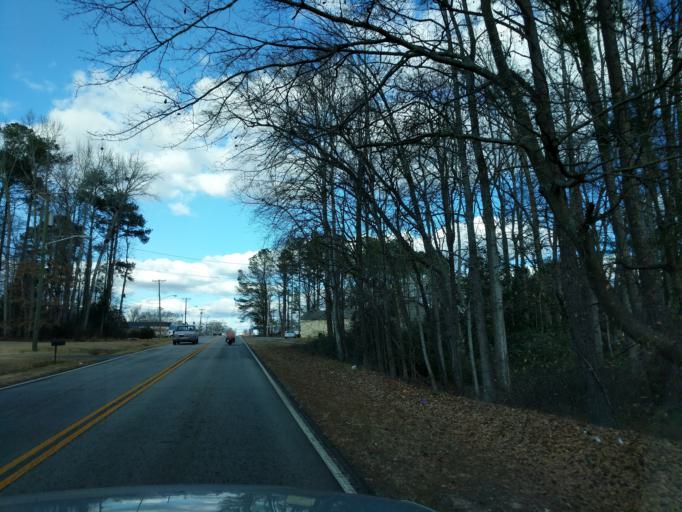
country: US
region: South Carolina
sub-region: Laurens County
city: Laurens
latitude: 34.4833
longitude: -82.0207
